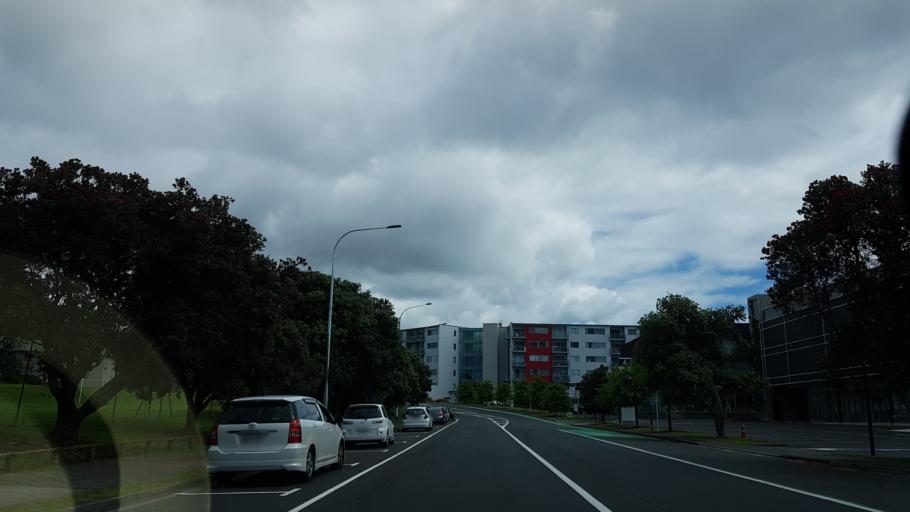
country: NZ
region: Auckland
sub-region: Auckland
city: North Shore
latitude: -36.7923
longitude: 174.7632
